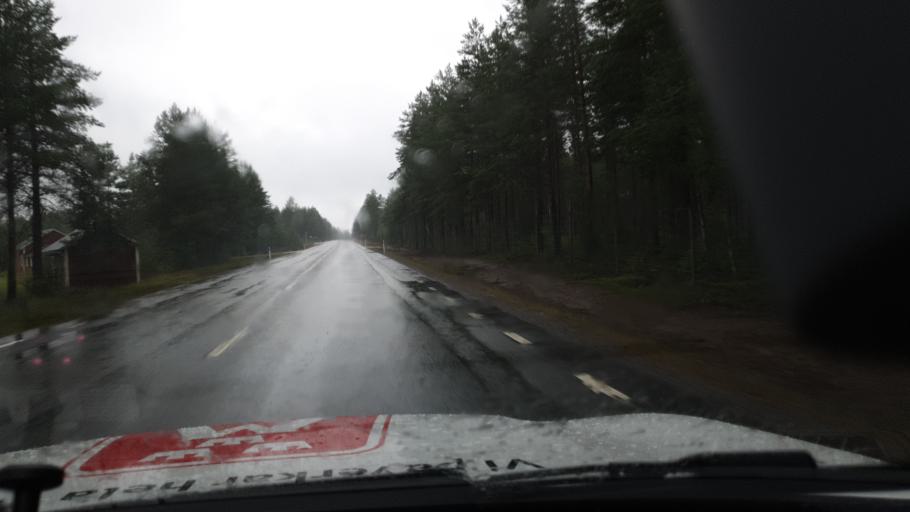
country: SE
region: Vaesterbotten
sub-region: Skelleftea Kommun
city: Burea
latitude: 64.5609
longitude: 21.2353
